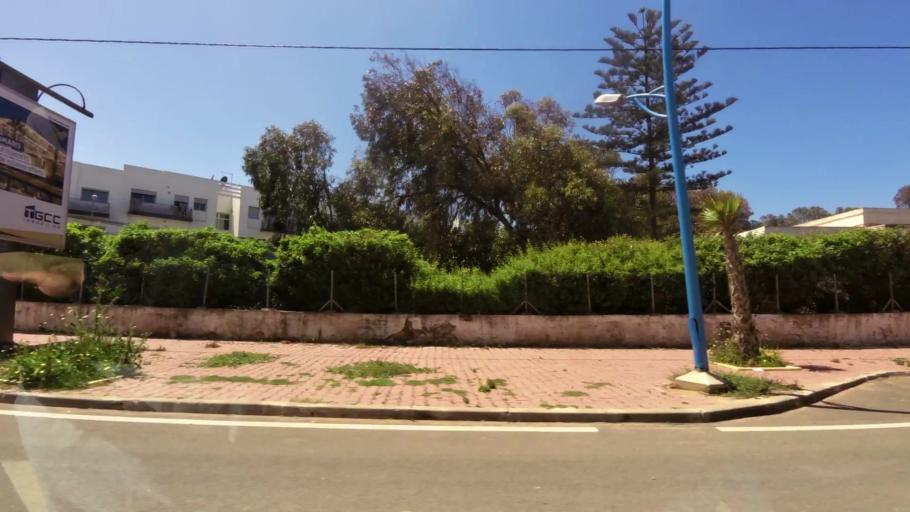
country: MA
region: Grand Casablanca
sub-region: Nouaceur
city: Dar Bouazza
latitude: 33.5311
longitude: -7.8214
